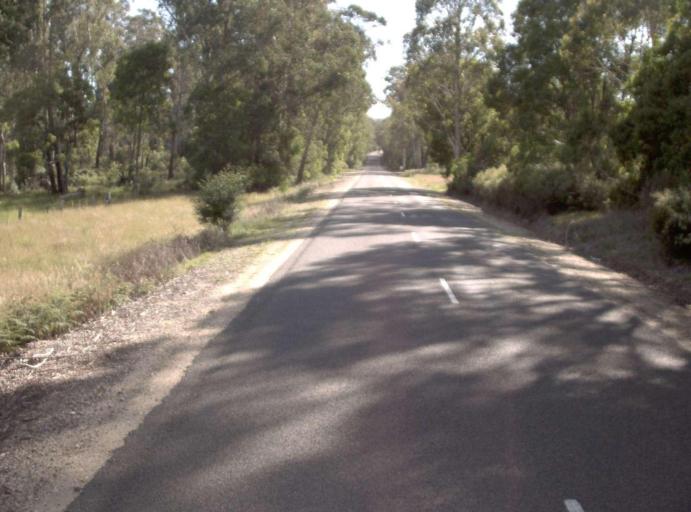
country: AU
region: Victoria
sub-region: East Gippsland
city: Lakes Entrance
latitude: -37.6684
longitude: 148.0641
